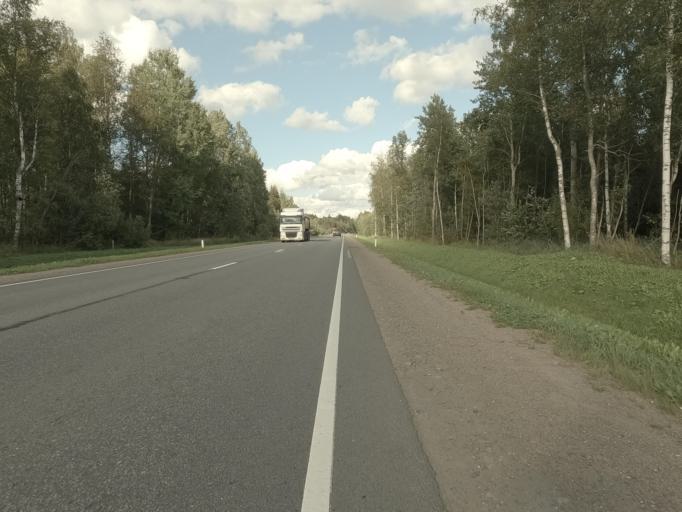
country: RU
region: Leningrad
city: Nikol'skoye
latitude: 59.6631
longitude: 30.8772
